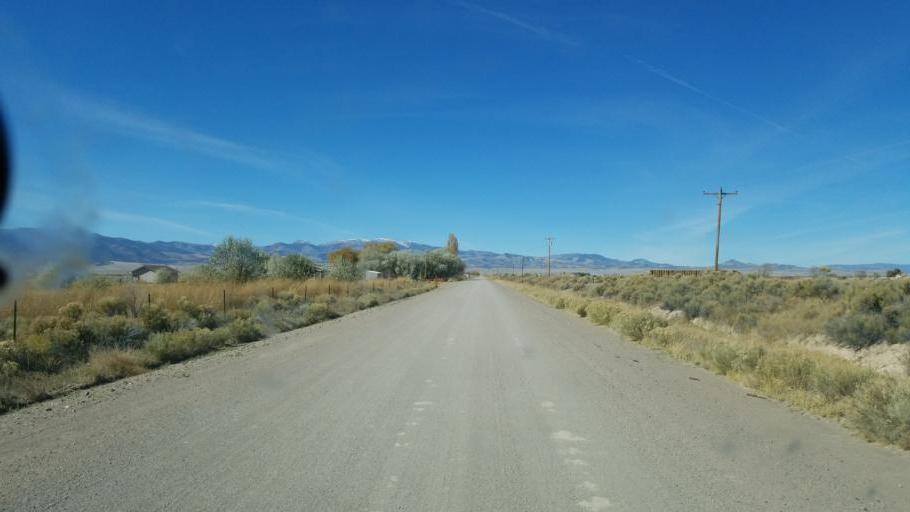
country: US
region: Colorado
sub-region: Rio Grande County
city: Monte Vista
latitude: 37.5313
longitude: -106.0813
